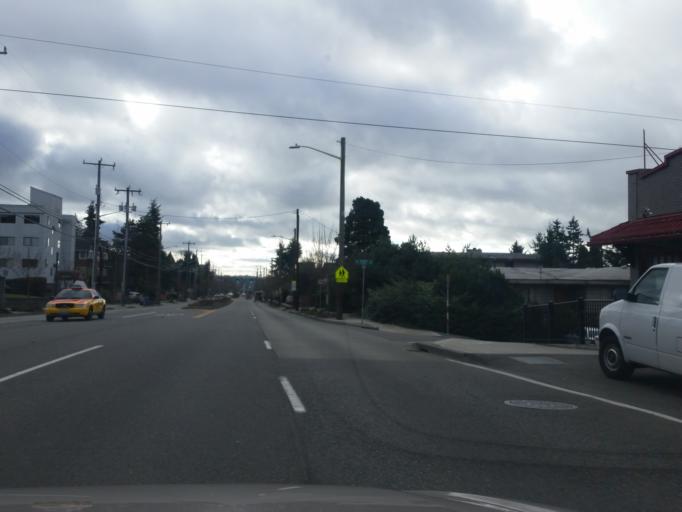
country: US
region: Washington
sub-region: King County
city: Shoreline
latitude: 47.7108
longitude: -122.3555
